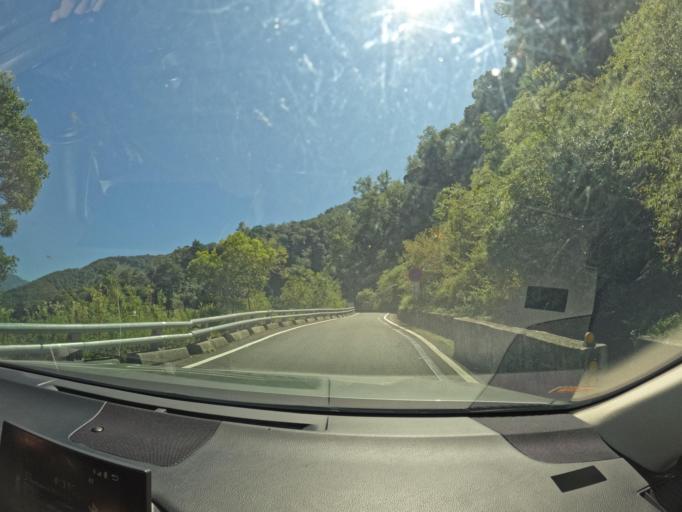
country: TW
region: Taiwan
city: Yujing
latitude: 23.2845
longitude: 120.8806
